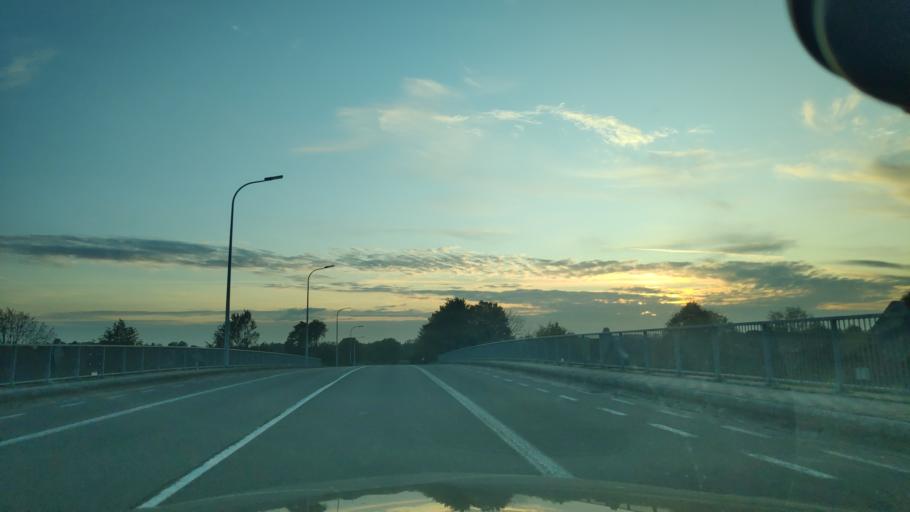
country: BE
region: Flanders
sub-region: Provincie Oost-Vlaanderen
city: Aalter
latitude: 51.0984
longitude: 3.4950
